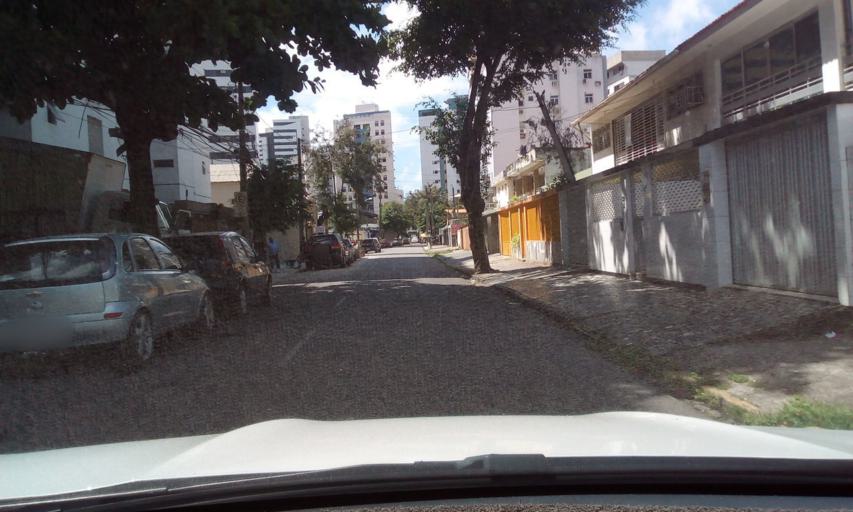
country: BR
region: Pernambuco
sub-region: Recife
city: Recife
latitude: -8.1320
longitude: -34.9048
